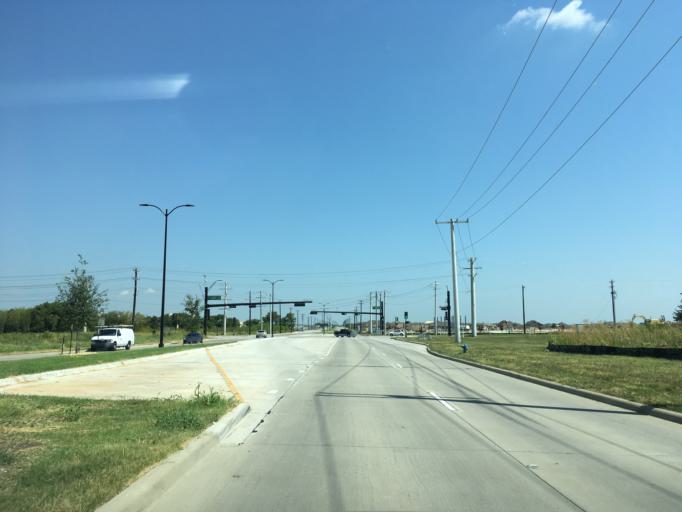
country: US
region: Texas
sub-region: Collin County
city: Prosper
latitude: 33.2024
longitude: -96.7676
